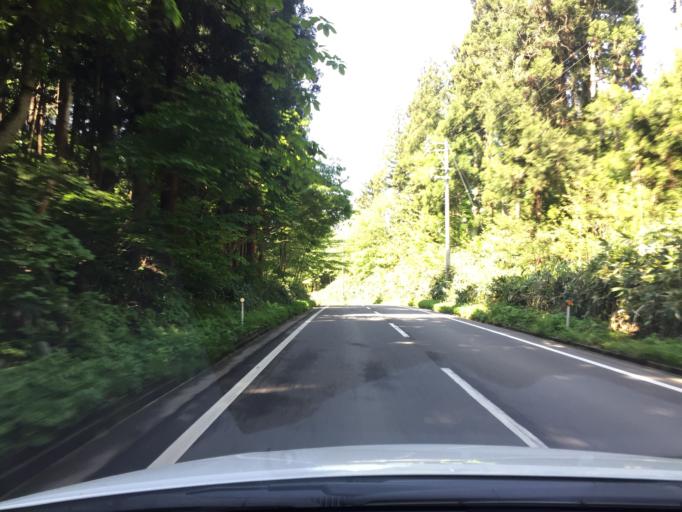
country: JP
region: Niigata
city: Kamo
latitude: 37.5599
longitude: 139.0794
